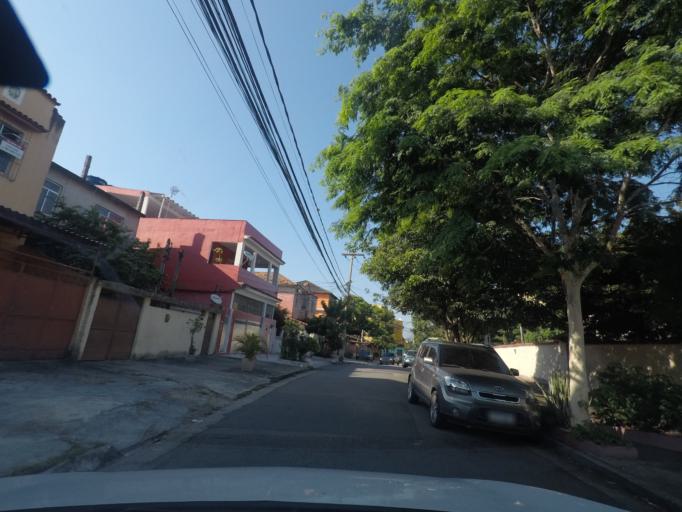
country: BR
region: Rio de Janeiro
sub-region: Duque De Caxias
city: Duque de Caxias
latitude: -22.8265
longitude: -43.2830
